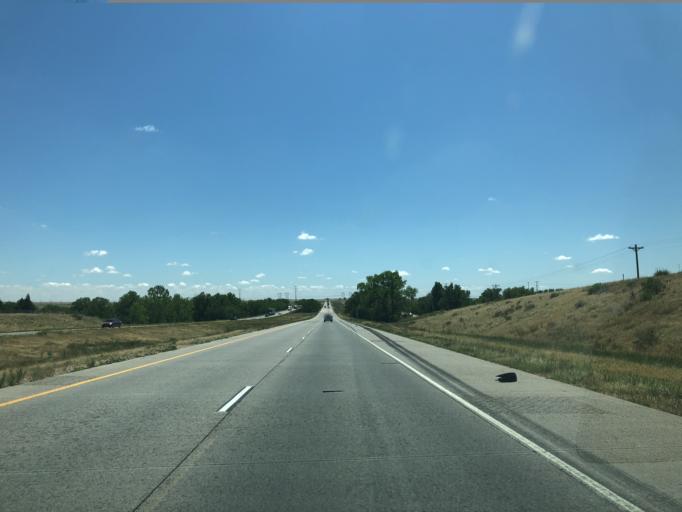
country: US
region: Colorado
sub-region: Arapahoe County
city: Byers
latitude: 39.6747
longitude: -104.1036
